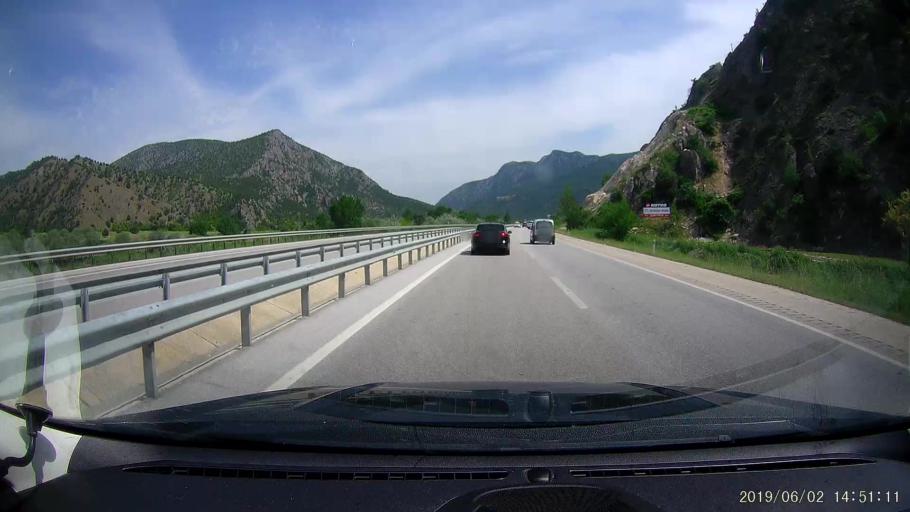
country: TR
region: Corum
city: Kargi
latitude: 41.0643
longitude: 34.5364
